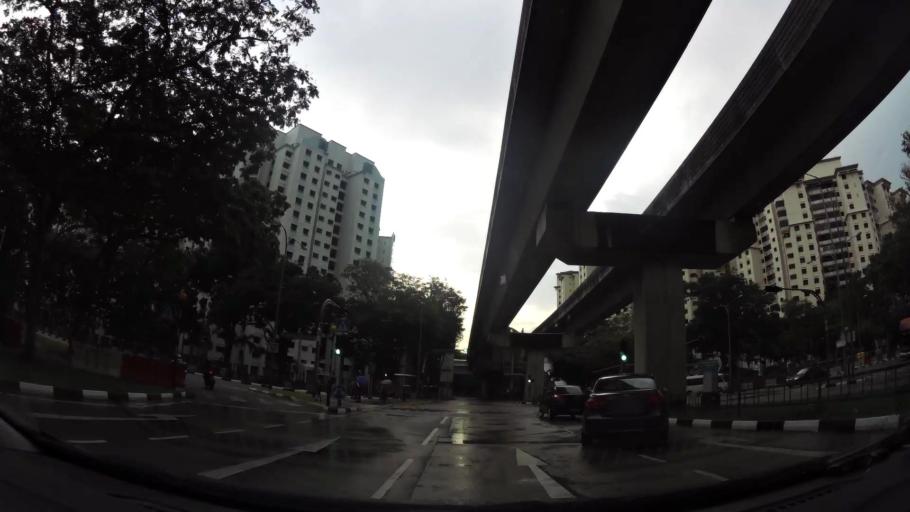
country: MY
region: Johor
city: Kampung Pasir Gudang Baru
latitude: 1.3887
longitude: 103.9063
